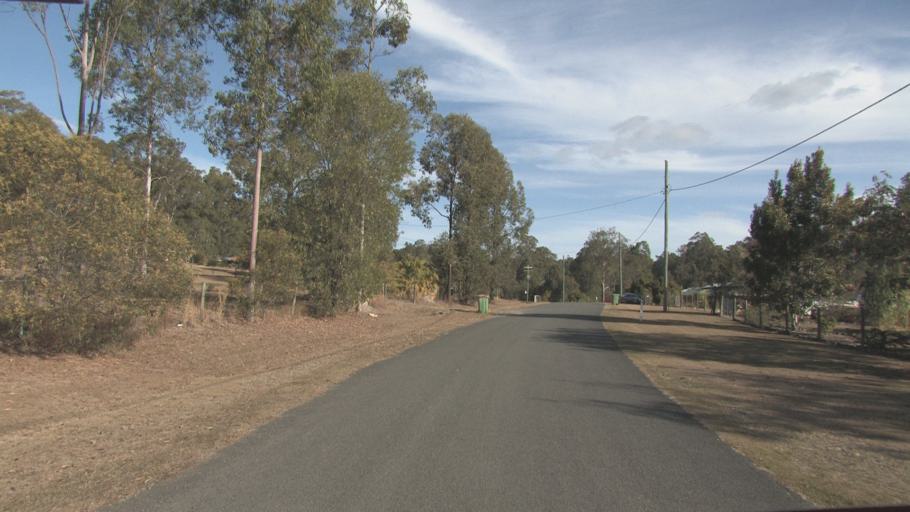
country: AU
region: Queensland
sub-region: Logan
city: Cedar Vale
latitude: -27.8739
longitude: 153.0087
